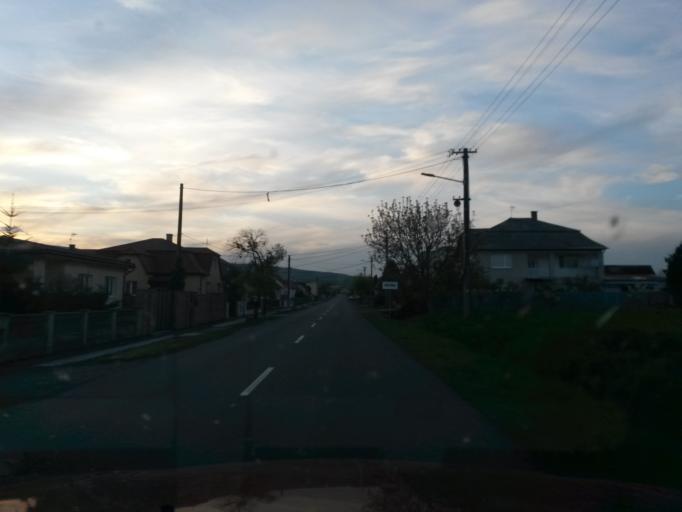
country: SK
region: Kosicky
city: Trebisov
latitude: 48.5468
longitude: 21.5614
